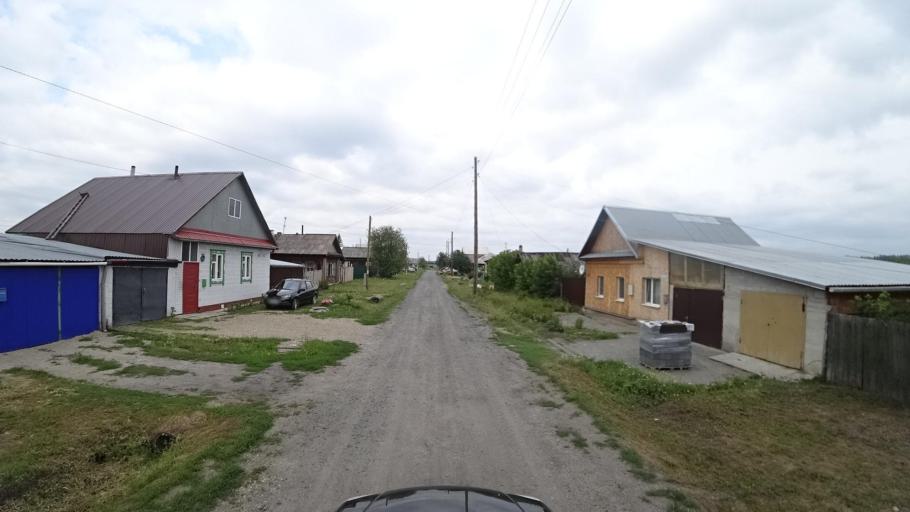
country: RU
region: Sverdlovsk
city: Kamyshlov
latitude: 56.8525
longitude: 62.6748
